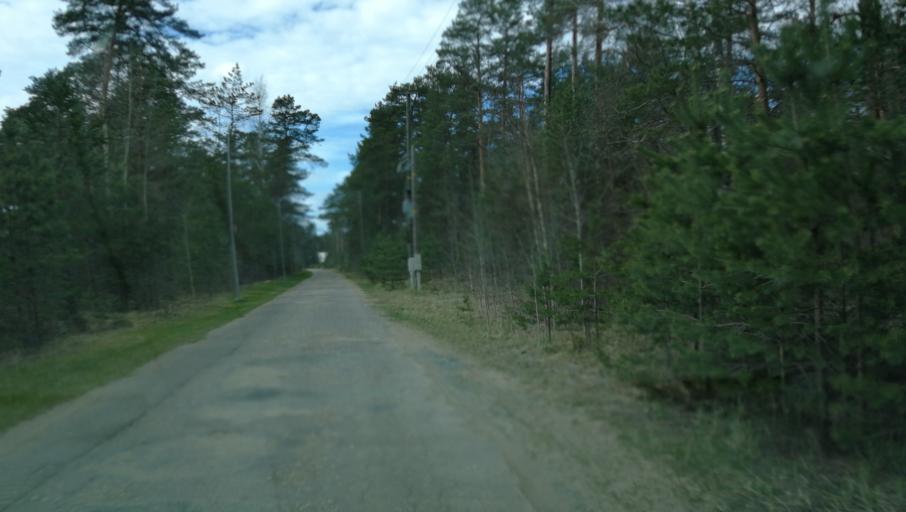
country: LV
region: Garkalne
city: Garkalne
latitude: 57.0391
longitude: 24.4394
